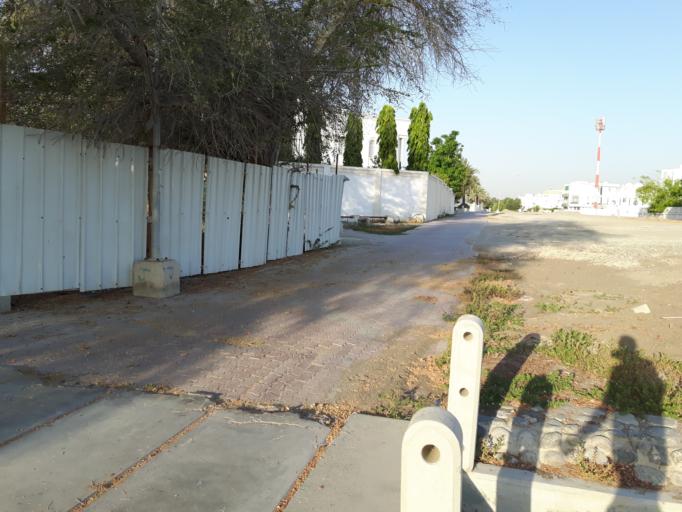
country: OM
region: Muhafazat Masqat
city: Bawshar
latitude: 23.6100
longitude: 58.4514
